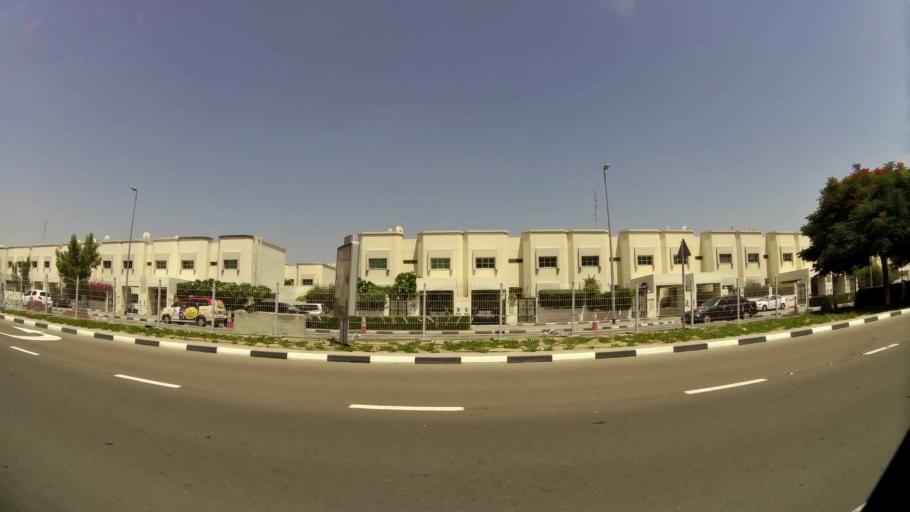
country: AE
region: Dubai
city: Dubai
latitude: 25.2120
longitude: 55.2626
